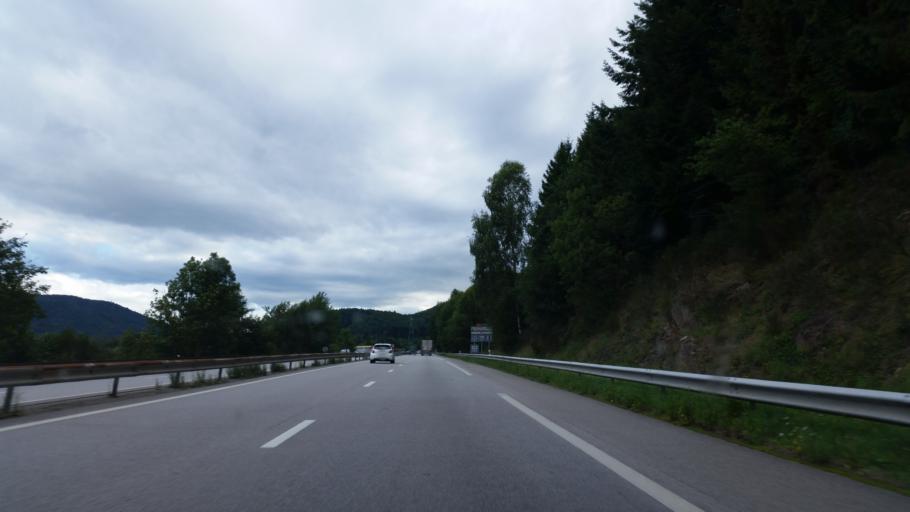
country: FR
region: Lorraine
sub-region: Departement des Vosges
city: Eloyes
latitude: 48.0840
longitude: 6.5960
